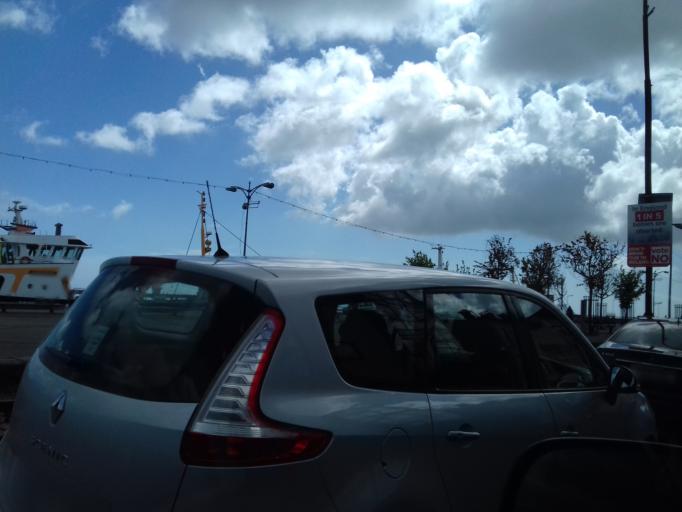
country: IE
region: Leinster
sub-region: Loch Garman
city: Loch Garman
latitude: 52.3398
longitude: -6.4605
